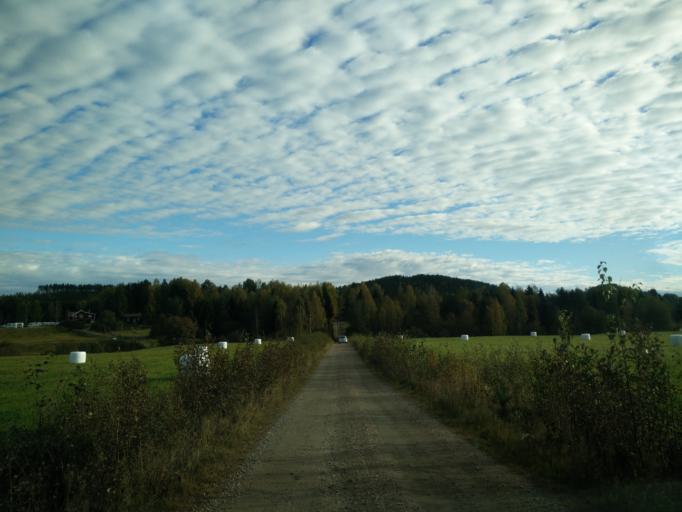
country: SE
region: Gaevleborg
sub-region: Bollnas Kommun
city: Kilafors
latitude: 61.3195
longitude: 16.7790
